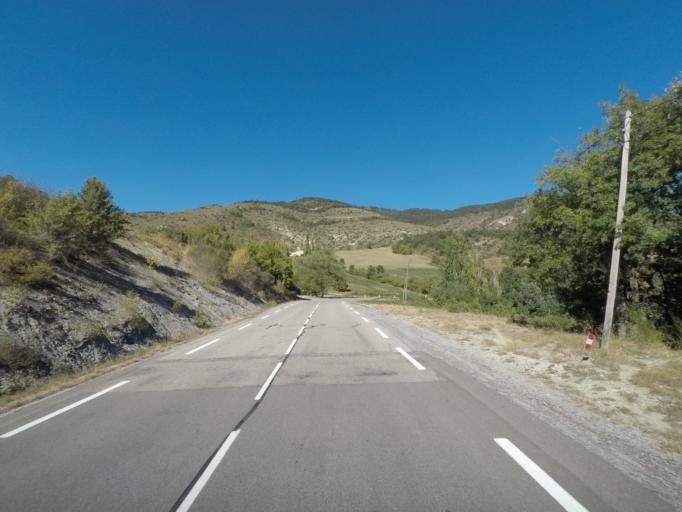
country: FR
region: Provence-Alpes-Cote d'Azur
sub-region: Departement des Hautes-Alpes
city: Serres
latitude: 44.4045
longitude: 5.5080
